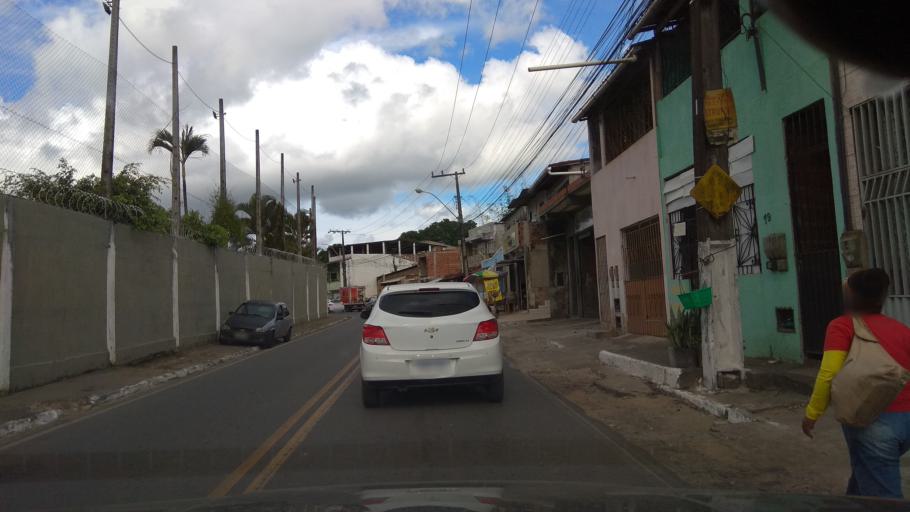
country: BR
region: Bahia
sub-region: Ilheus
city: Ilheus
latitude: -14.7934
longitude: -39.0633
